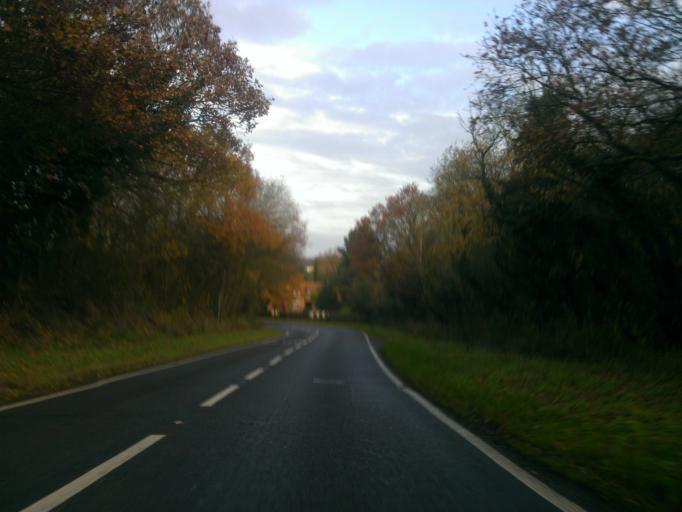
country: GB
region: England
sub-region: Essex
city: Great Bentley
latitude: 51.8286
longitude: 1.0663
